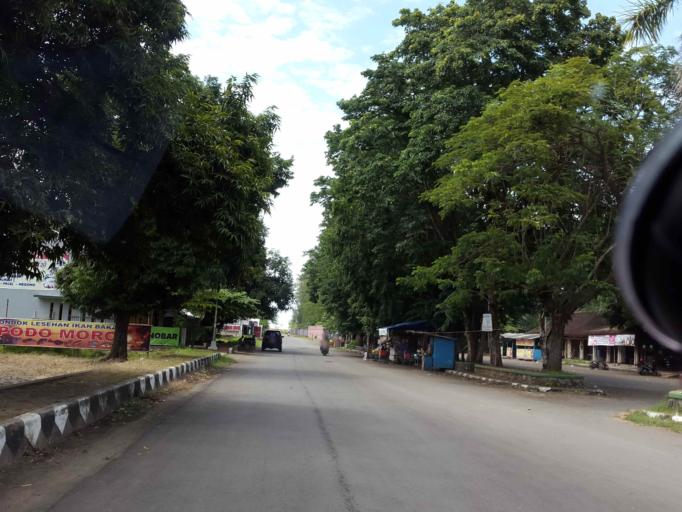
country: ID
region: Central Java
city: Pemalang
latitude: -6.8646
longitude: 109.3803
